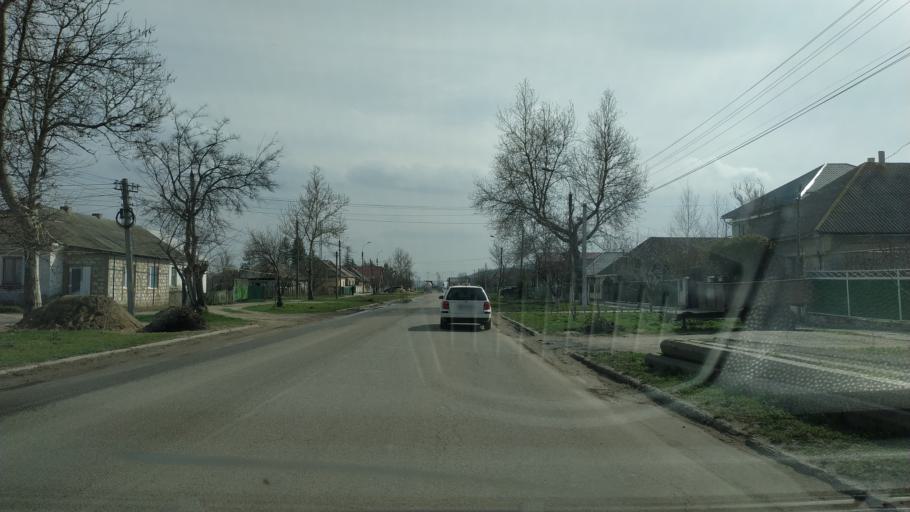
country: MD
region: Gagauzia
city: Vulcanesti
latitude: 45.6795
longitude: 28.4096
